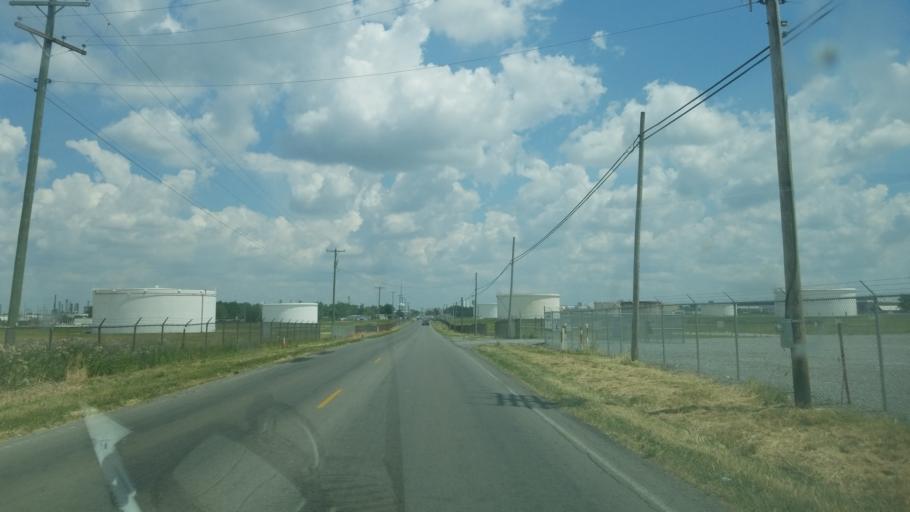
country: US
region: Ohio
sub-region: Allen County
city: Fort Shawnee
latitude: 40.7022
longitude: -84.1213
